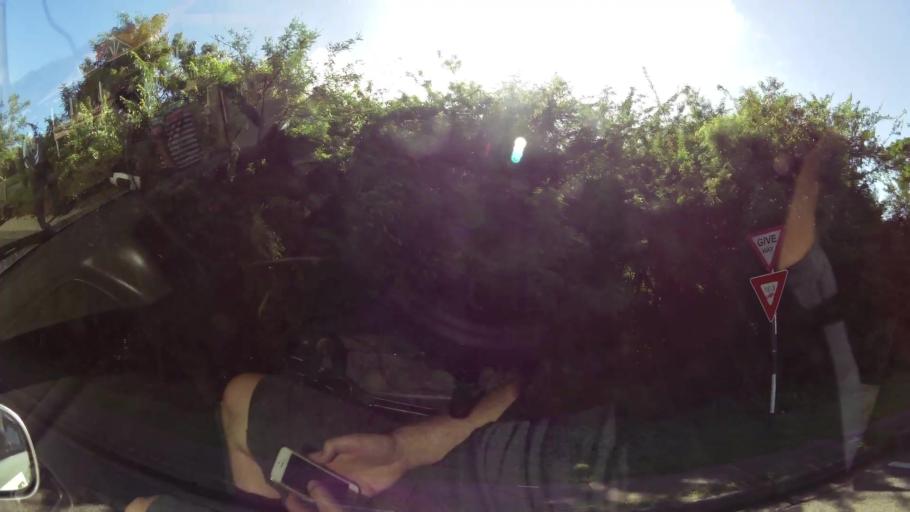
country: GD
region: Saint George
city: Saint George's
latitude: 12.0044
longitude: -61.7683
